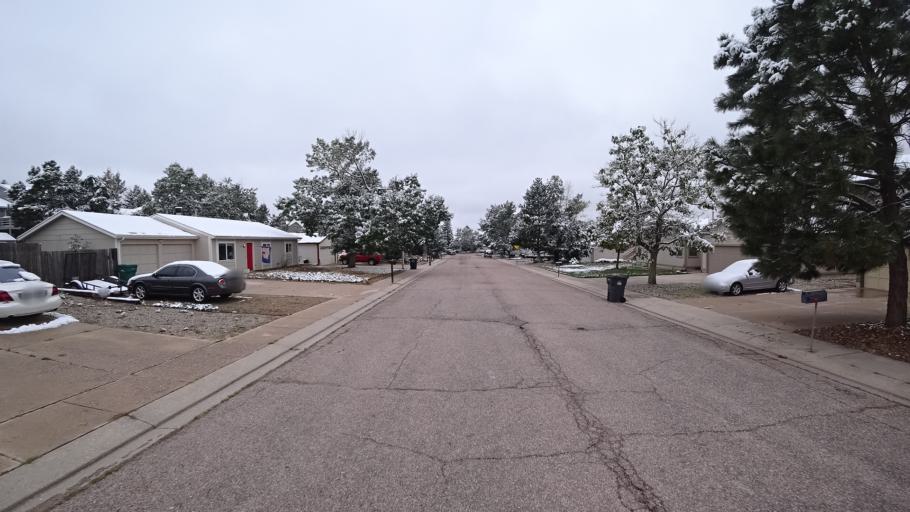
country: US
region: Colorado
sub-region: El Paso County
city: Cimarron Hills
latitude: 38.9242
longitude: -104.7730
